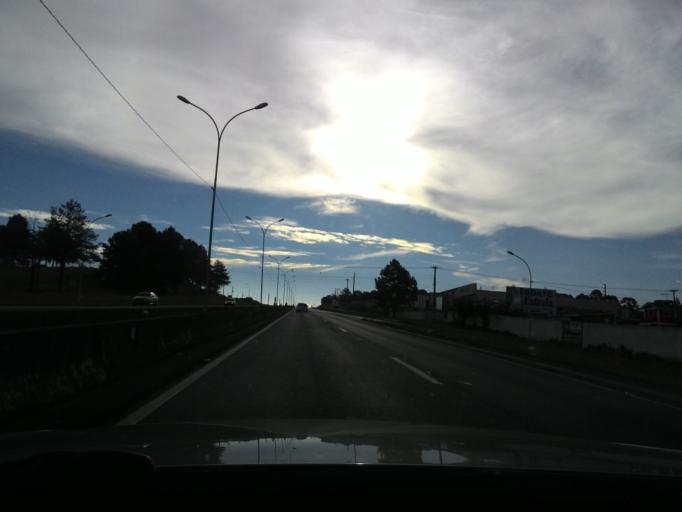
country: BR
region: Parana
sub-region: Quatro Barras
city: Quatro Barras
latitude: -25.3714
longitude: -49.1302
